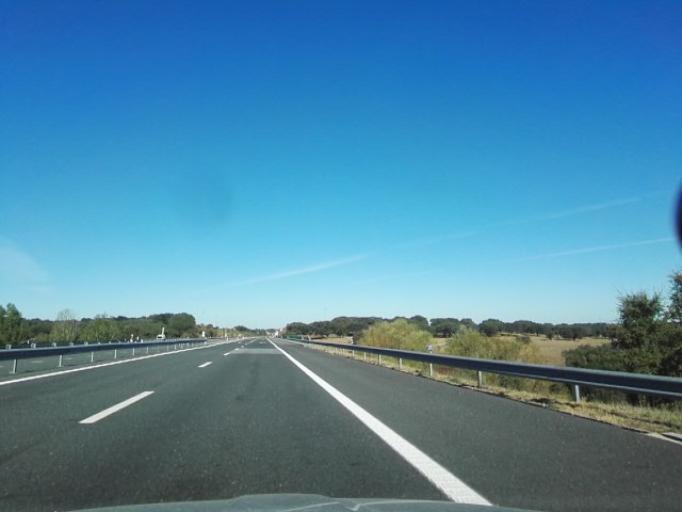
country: PT
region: Evora
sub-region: Arraiolos
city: Arraiolos
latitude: 38.6145
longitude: -8.0713
